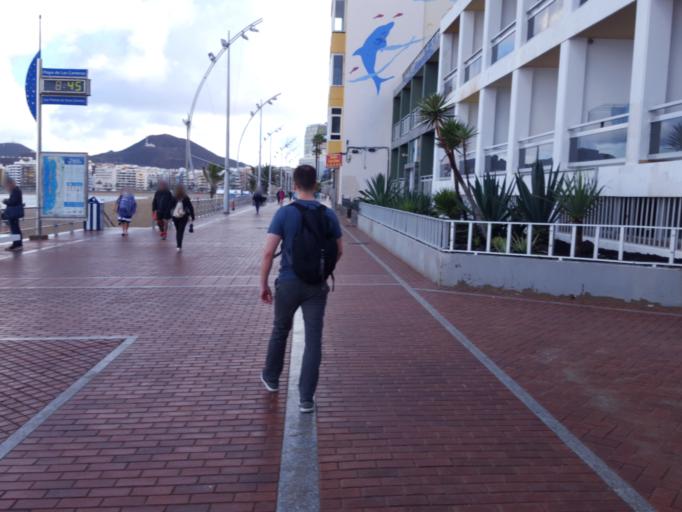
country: ES
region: Canary Islands
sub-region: Provincia de Las Palmas
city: Las Palmas de Gran Canaria
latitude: 28.1415
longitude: -15.4348
